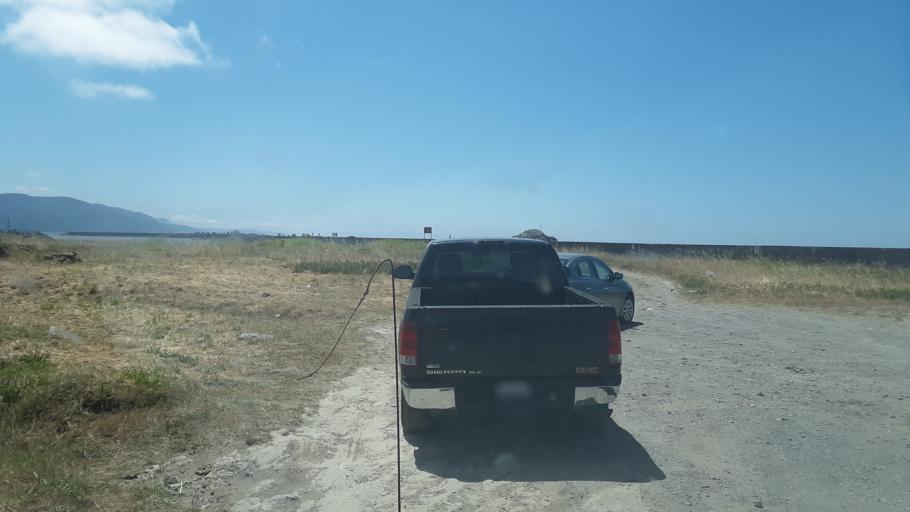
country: US
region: California
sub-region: Del Norte County
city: Crescent City
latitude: 41.7460
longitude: -124.2001
